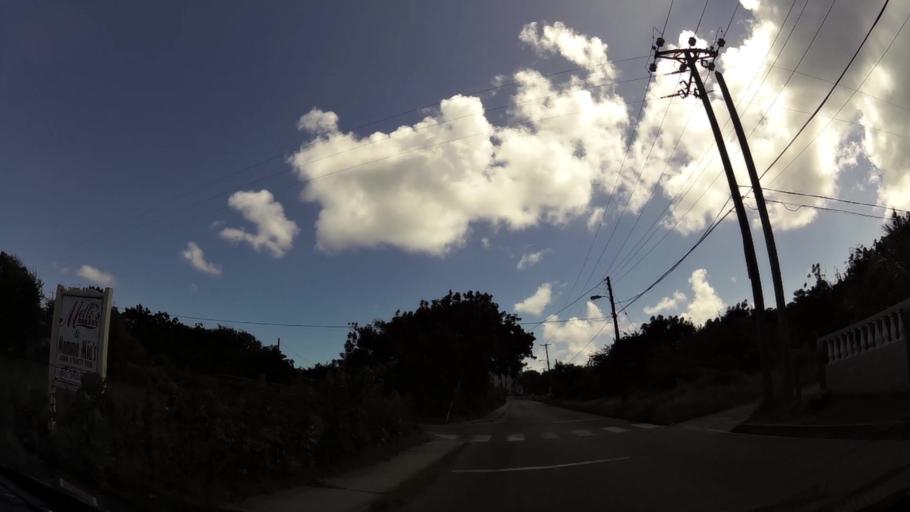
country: VG
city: Tortola
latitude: 18.4437
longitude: -64.4361
